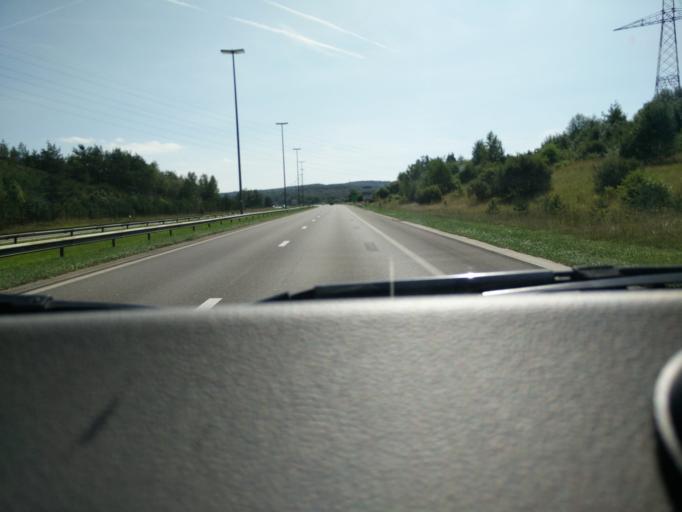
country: BE
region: Wallonia
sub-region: Province du Luxembourg
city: Arlon
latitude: 49.6782
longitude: 5.7616
